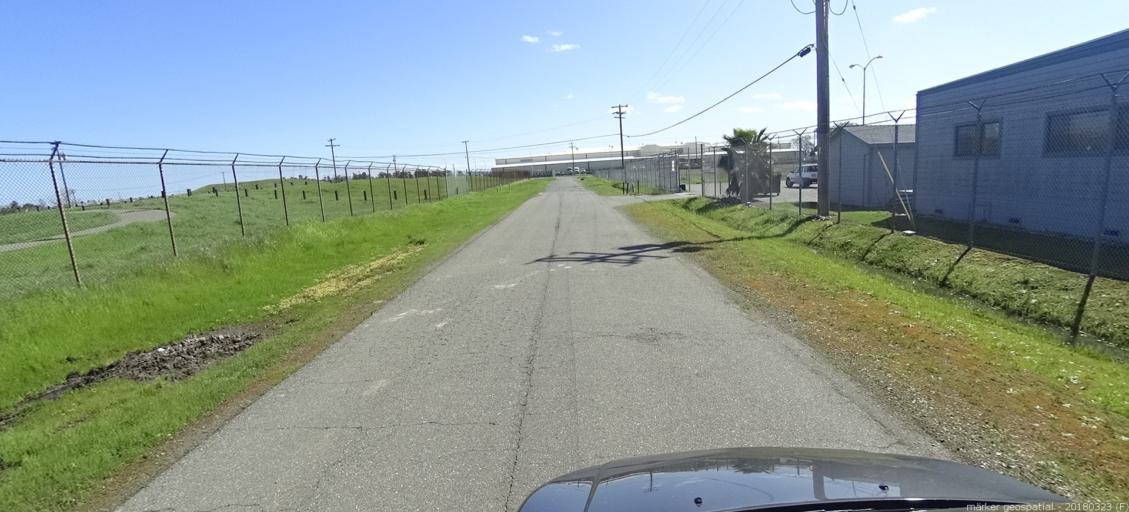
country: US
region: California
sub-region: Sacramento County
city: Rio Linda
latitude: 38.6690
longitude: -121.4172
